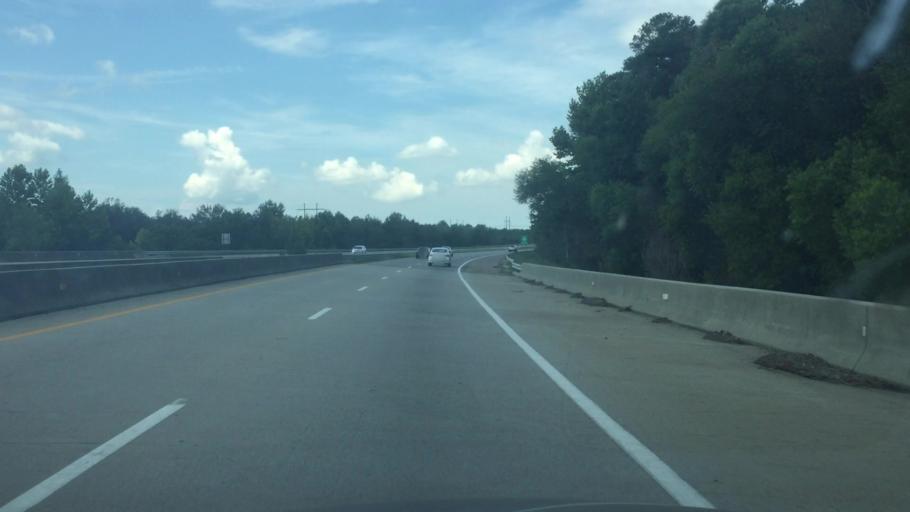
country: US
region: North Carolina
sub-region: Richmond County
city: Hamlet
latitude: 34.8525
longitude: -79.7289
